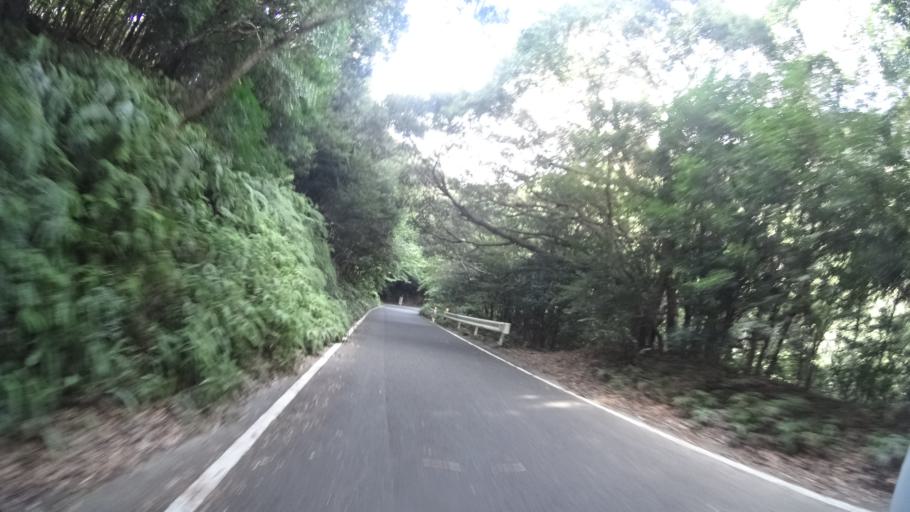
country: JP
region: Kagoshima
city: Nishinoomote
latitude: 30.3392
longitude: 130.3939
